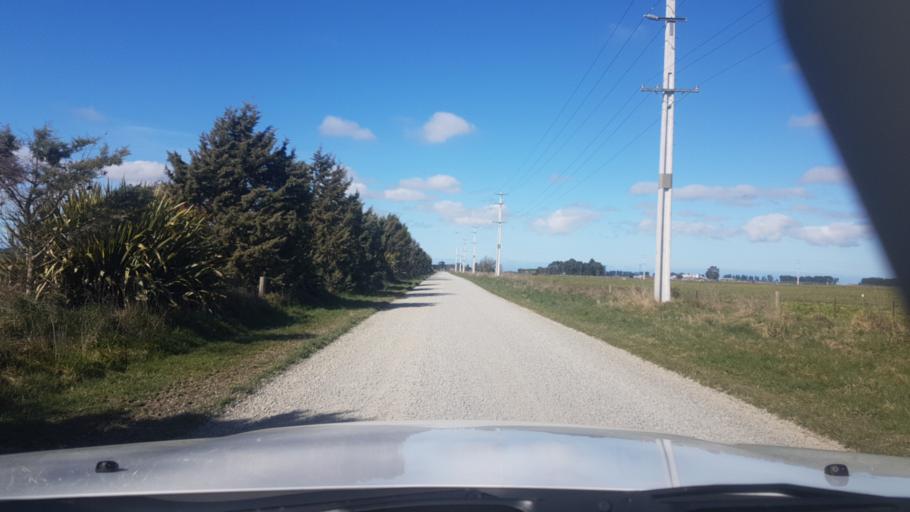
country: NZ
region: Canterbury
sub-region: Timaru District
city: Pleasant Point
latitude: -44.0973
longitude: 171.3879
